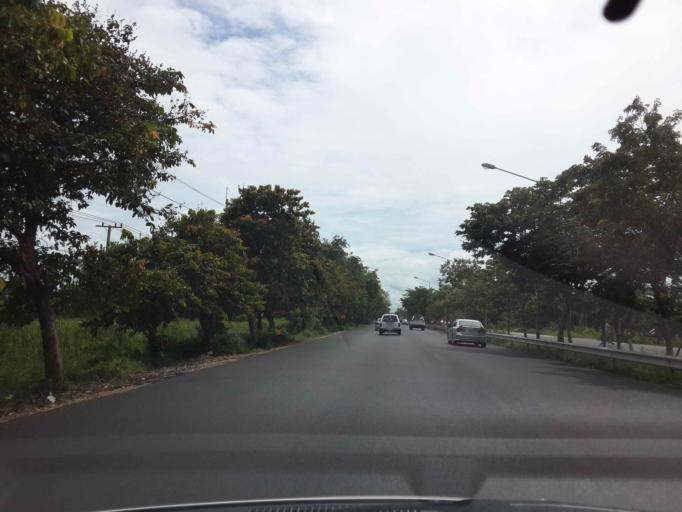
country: TH
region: Ratchaburi
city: Pak Tho
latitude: 13.4429
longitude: 99.8033
